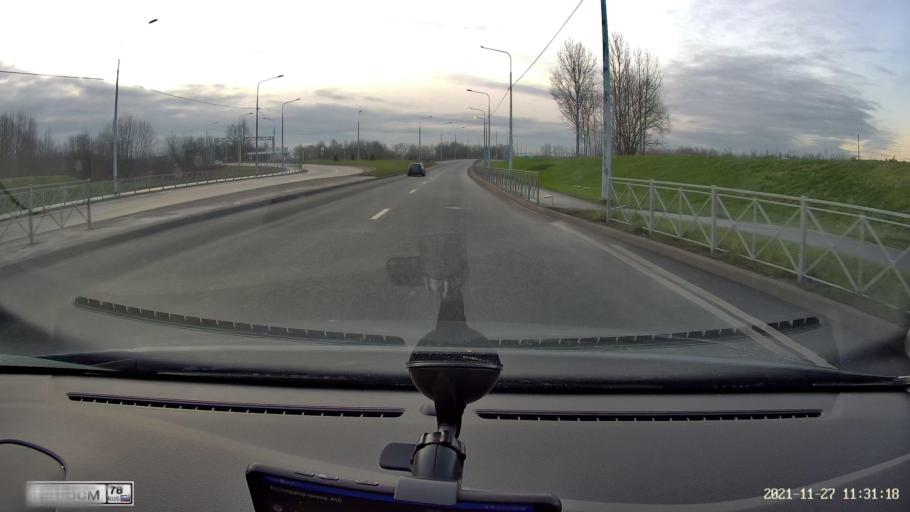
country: RU
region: St.-Petersburg
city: Krasnoye Selo
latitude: 59.7211
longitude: 30.0509
